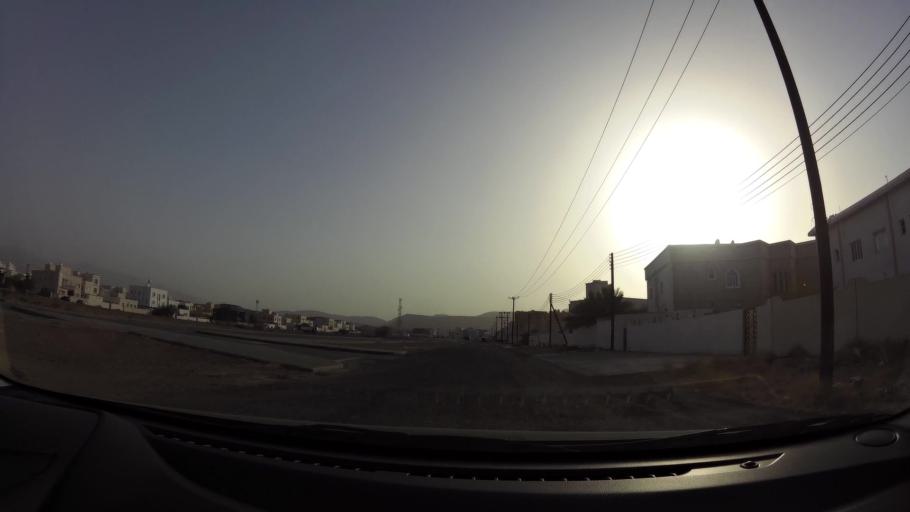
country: OM
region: Muhafazat Masqat
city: Bawshar
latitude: 23.5314
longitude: 58.3514
